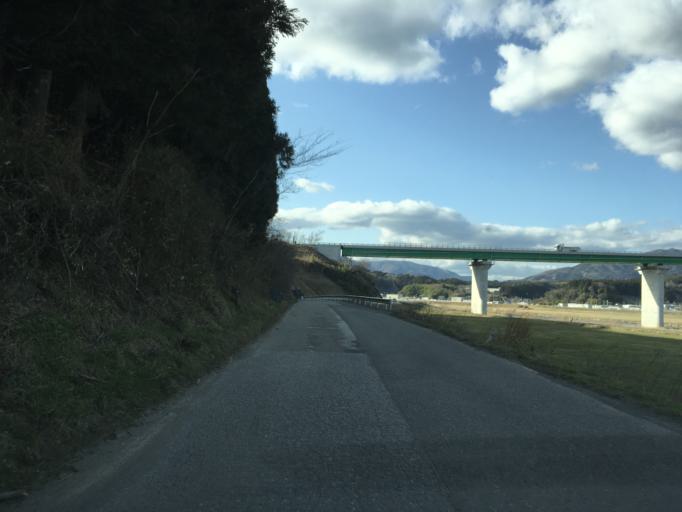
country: JP
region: Iwate
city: Ofunato
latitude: 39.0244
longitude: 141.6157
